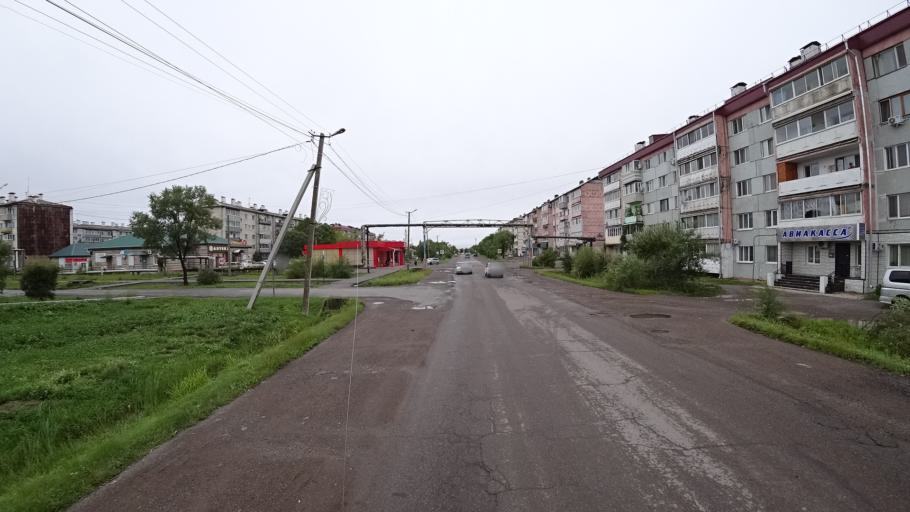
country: RU
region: Primorskiy
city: Monastyrishche
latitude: 44.2035
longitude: 132.4486
